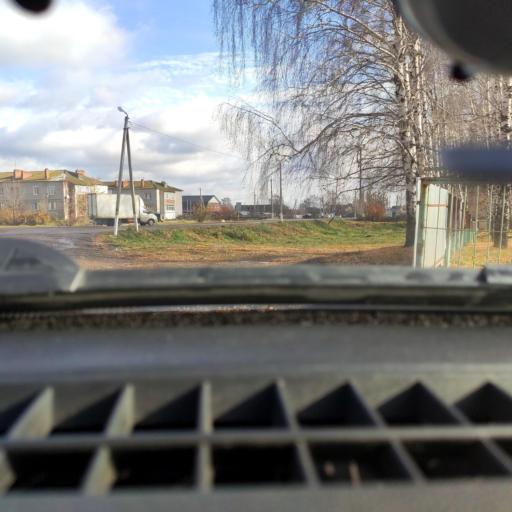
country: RU
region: Bashkortostan
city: Mikhaylovka
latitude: 54.7821
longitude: 55.8357
